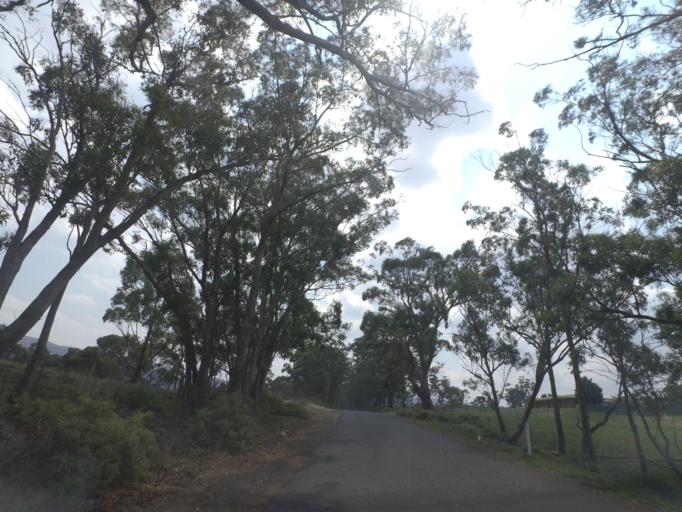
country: AU
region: Victoria
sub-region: Moorabool
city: Bacchus Marsh
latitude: -37.6162
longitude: 144.4413
